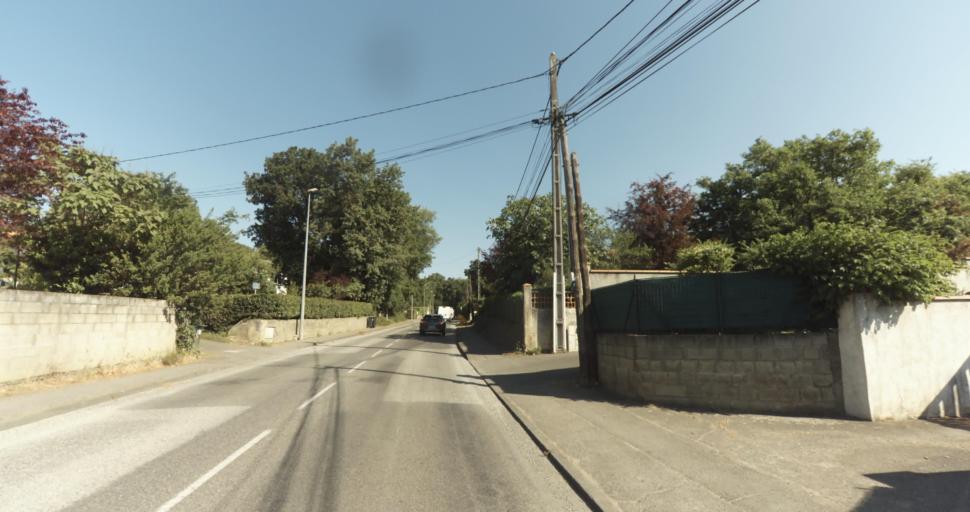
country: FR
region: Midi-Pyrenees
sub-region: Departement de la Haute-Garonne
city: Plaisance-du-Touch
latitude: 43.5709
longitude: 1.2936
